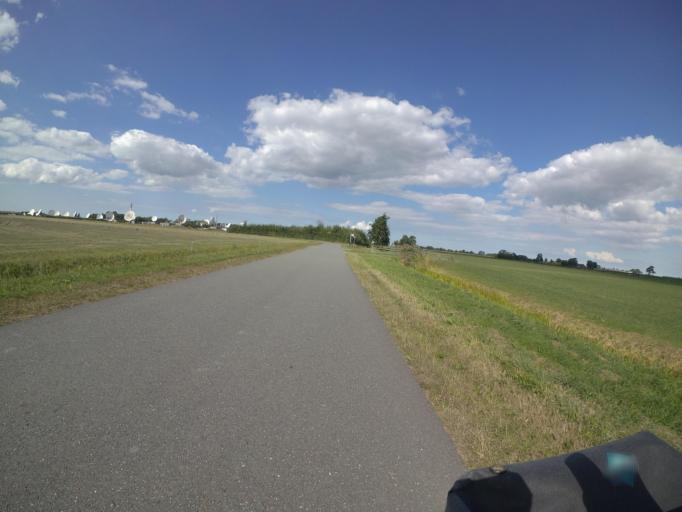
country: NL
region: Friesland
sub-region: Gemeente Kollumerland en Nieuwkruisland
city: Kollum
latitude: 53.2809
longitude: 6.2216
